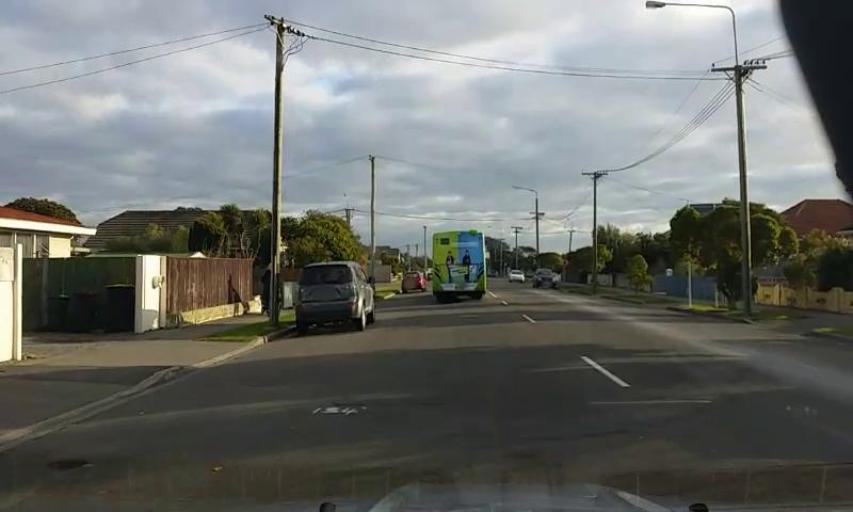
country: NZ
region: Canterbury
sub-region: Christchurch City
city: Christchurch
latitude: -43.5225
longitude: 172.7323
